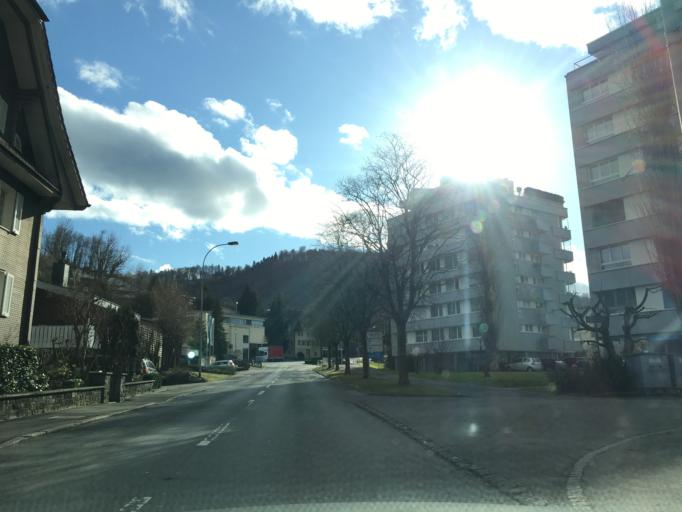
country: CH
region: Lucerne
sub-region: Lucerne-Land District
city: Ebikon
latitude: 47.0780
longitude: 8.3375
